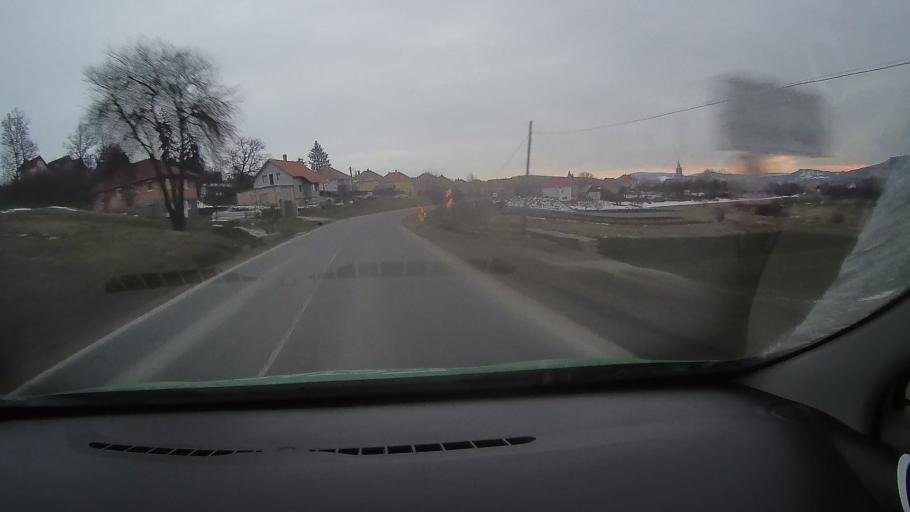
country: RO
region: Harghita
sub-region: Comuna Feliceni
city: Feliceni
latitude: 46.2769
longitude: 25.2855
